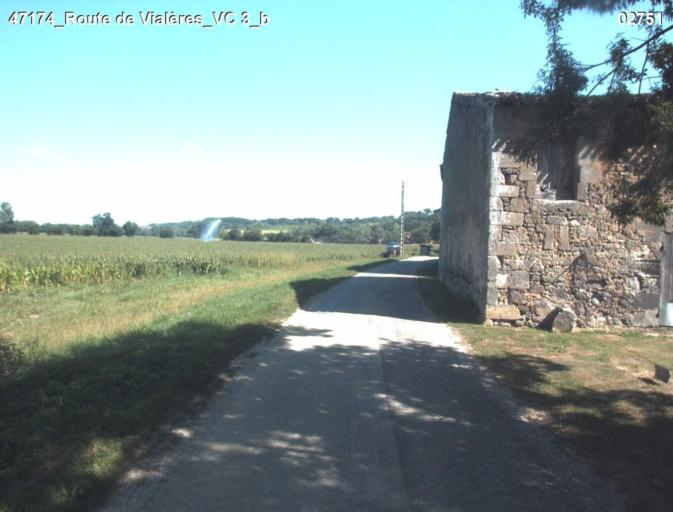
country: FR
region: Aquitaine
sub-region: Departement du Lot-et-Garonne
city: Nerac
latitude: 44.0570
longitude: 0.3857
